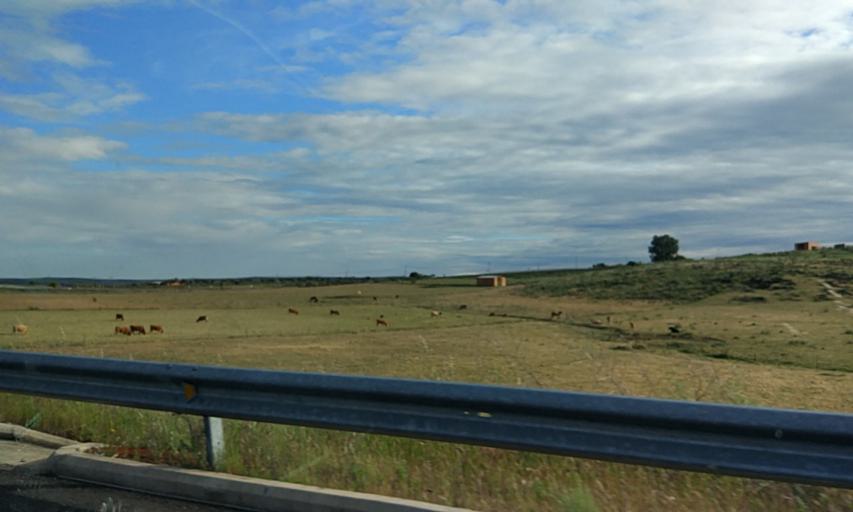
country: ES
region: Extremadura
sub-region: Provincia de Caceres
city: Casas de Don Gomez
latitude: 40.0176
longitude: -6.5896
